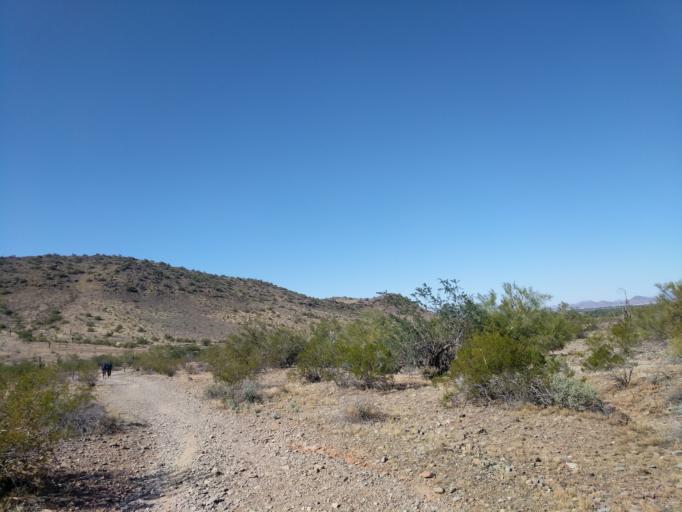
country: US
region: Arizona
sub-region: Maricopa County
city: Glendale
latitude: 33.5937
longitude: -112.0719
